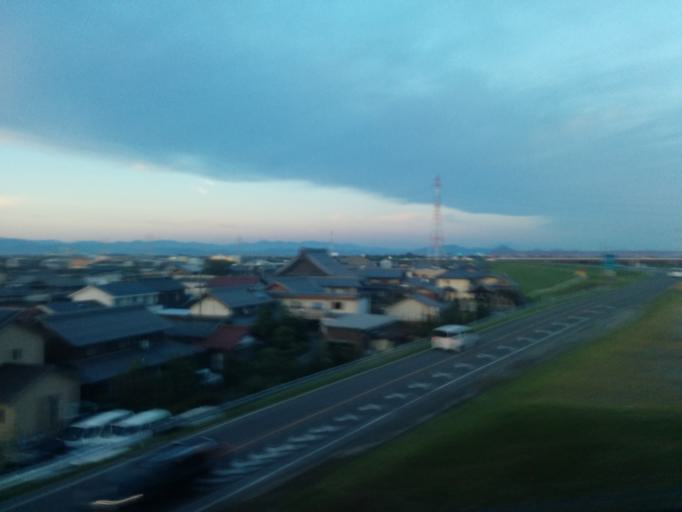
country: JP
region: Gifu
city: Ogaki
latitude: 35.3421
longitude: 136.6466
